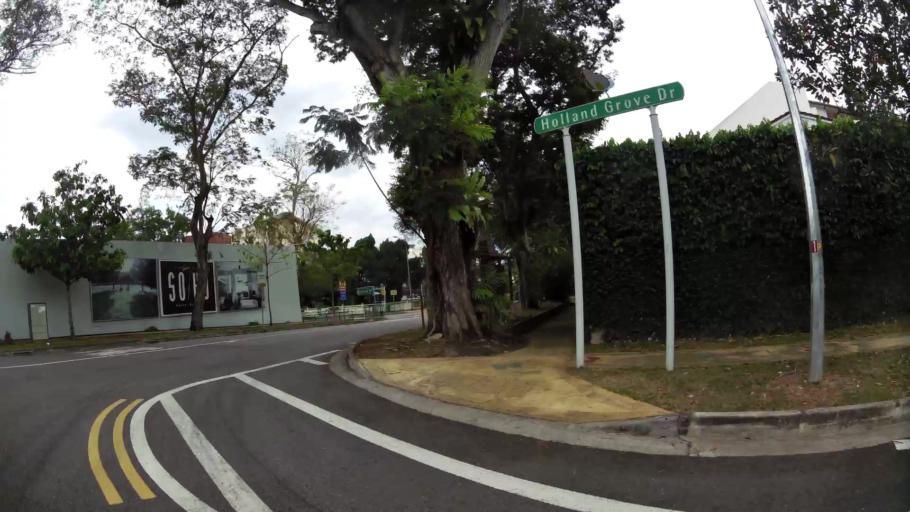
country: SG
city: Singapore
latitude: 1.3156
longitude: 103.7828
